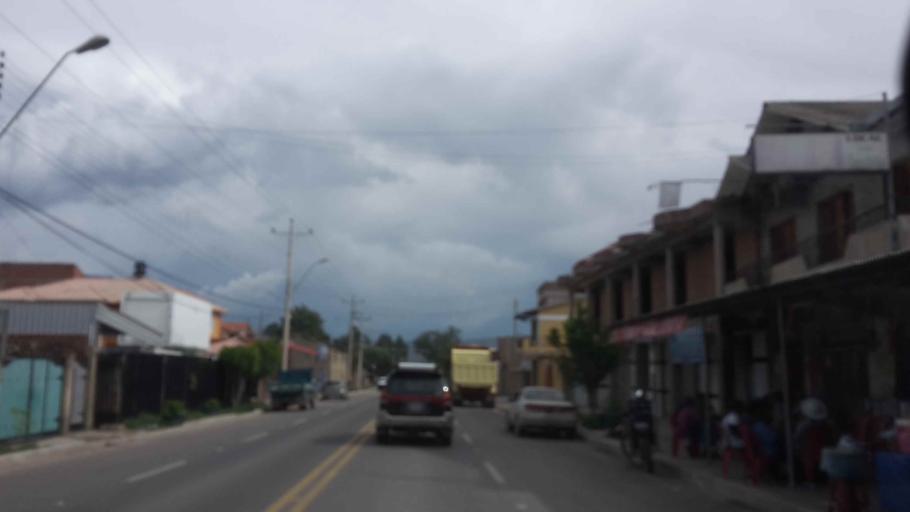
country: BO
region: Cochabamba
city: Cochabamba
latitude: -17.3613
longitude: -66.2531
